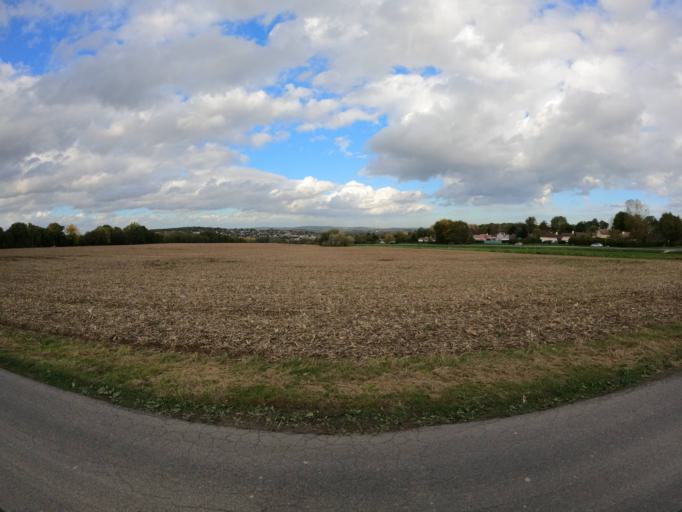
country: FR
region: Ile-de-France
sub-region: Departement de Seine-et-Marne
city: Coupvray
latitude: 48.8879
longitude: 2.8059
